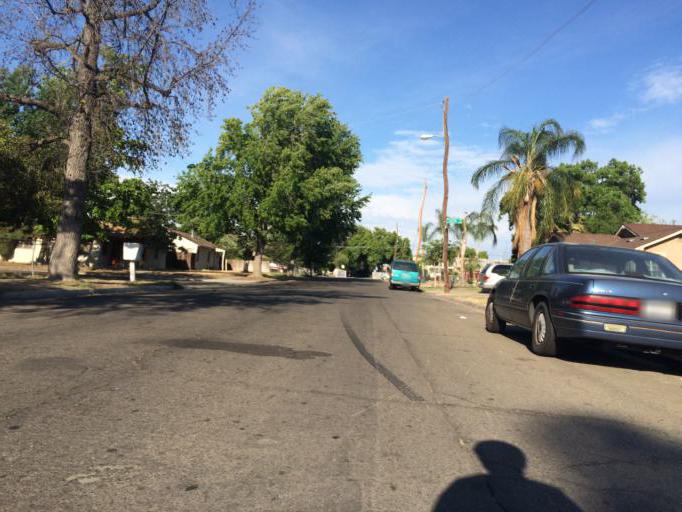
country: US
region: California
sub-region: Fresno County
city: Fresno
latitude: 36.7632
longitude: -119.7651
